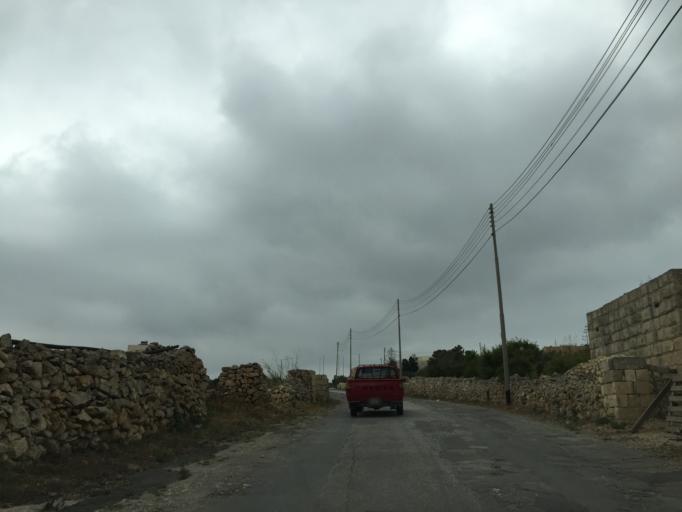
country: MT
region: L-Imgarr
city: Imgarr
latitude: 35.9178
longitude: 14.3724
